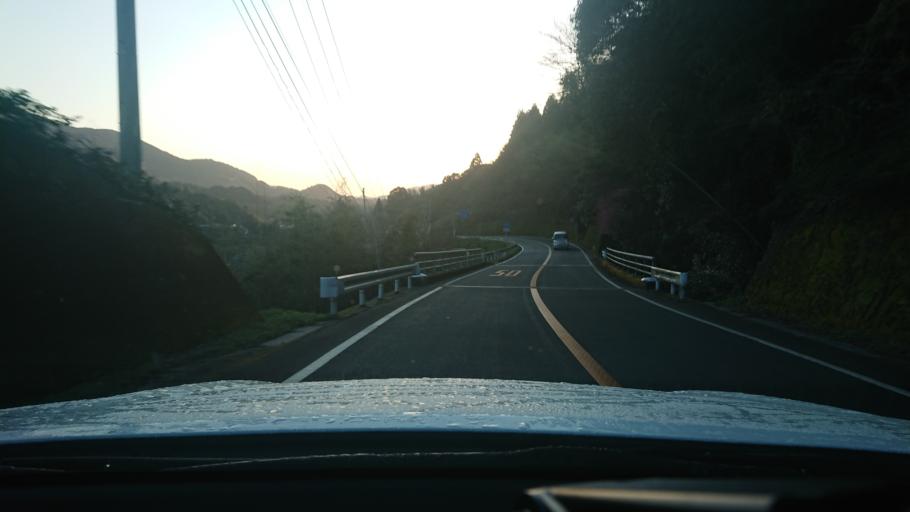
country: JP
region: Tokushima
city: Ishii
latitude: 33.9334
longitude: 134.4544
